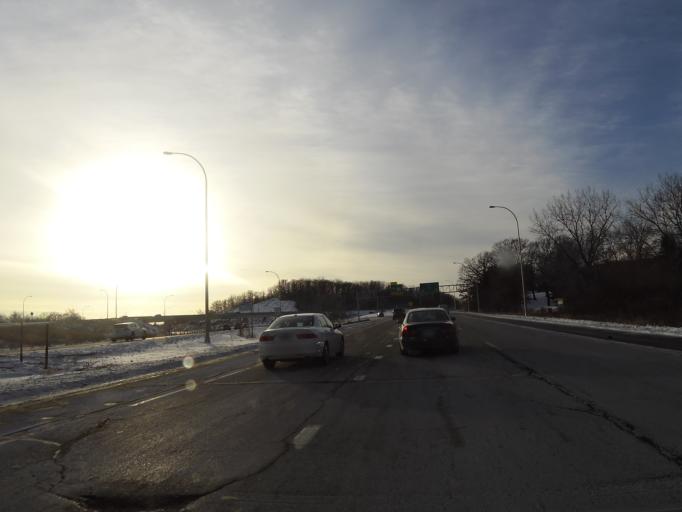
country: US
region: Minnesota
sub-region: Hennepin County
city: Edina
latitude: 44.8905
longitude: -93.4044
